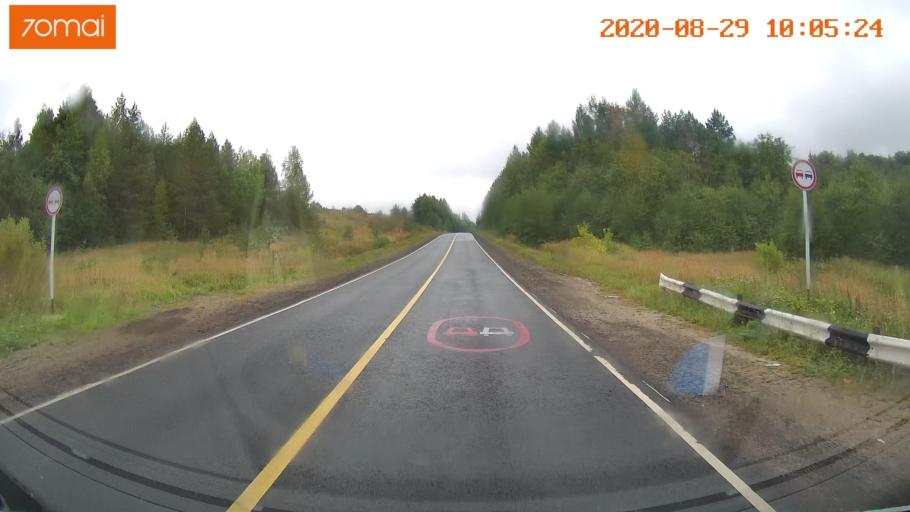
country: RU
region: Ivanovo
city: Zarechnyy
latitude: 57.3929
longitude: 42.5205
